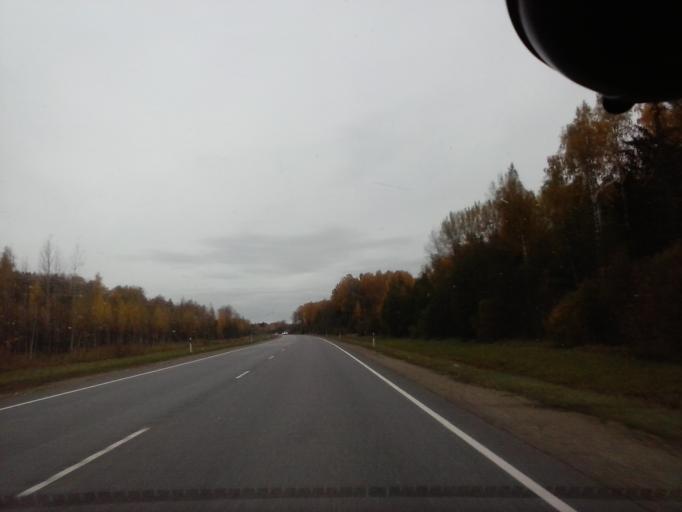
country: EE
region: Tartu
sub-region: Puhja vald
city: Puhja
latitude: 58.5019
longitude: 26.3297
